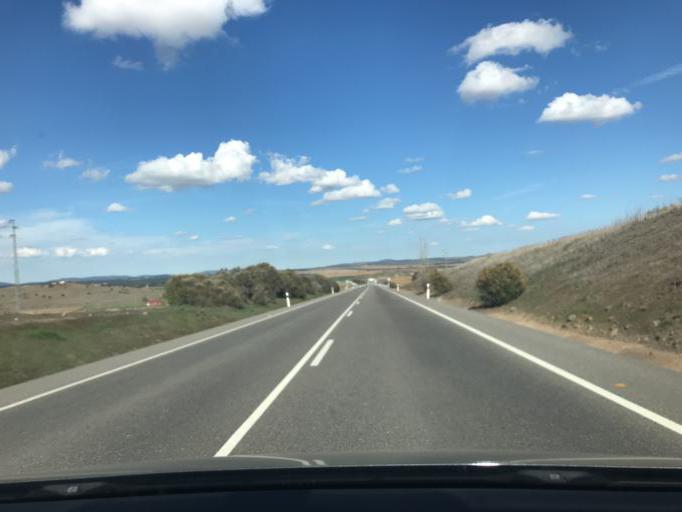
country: ES
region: Andalusia
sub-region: Province of Cordoba
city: Fuente Obejuna
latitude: 38.2673
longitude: -5.4344
